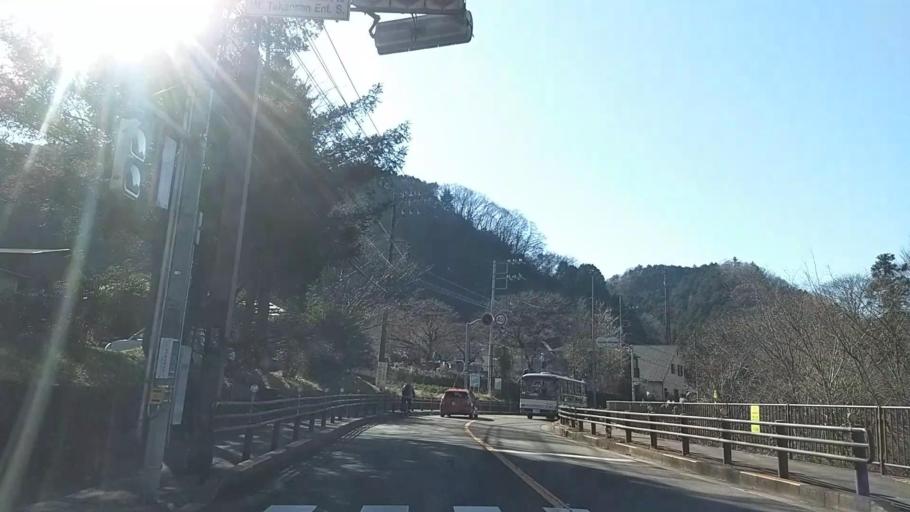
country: JP
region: Tokyo
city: Hachioji
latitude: 35.6293
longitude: 139.2693
